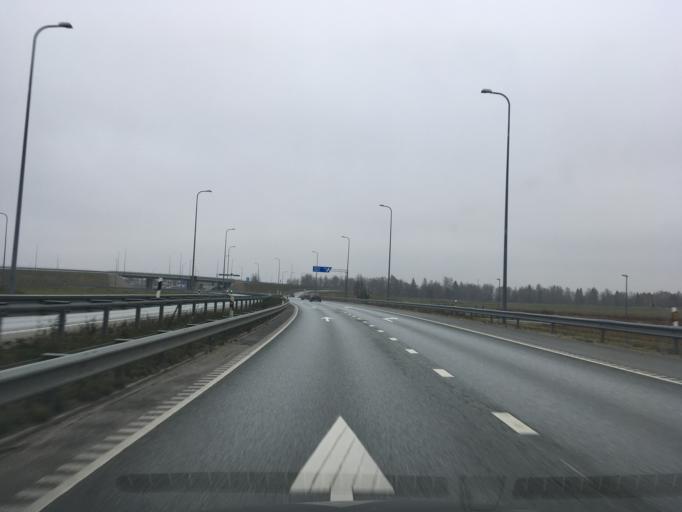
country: EE
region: Ida-Virumaa
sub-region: Johvi vald
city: Johvi
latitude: 59.3702
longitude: 27.3857
